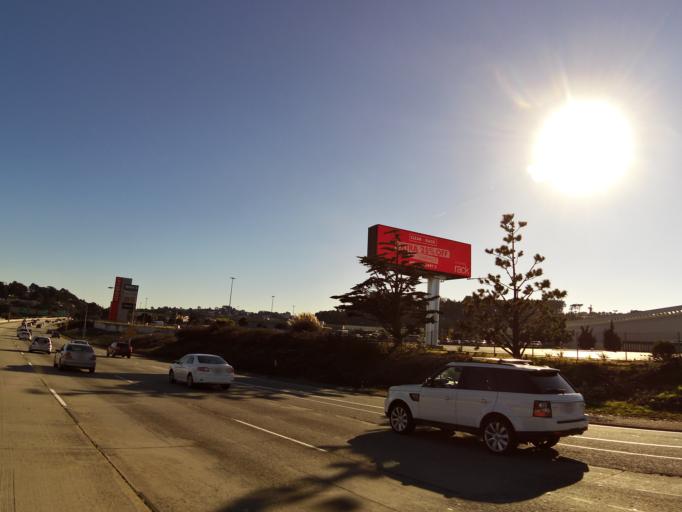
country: US
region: California
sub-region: San Mateo County
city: Colma
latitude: 37.6750
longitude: -122.4695
